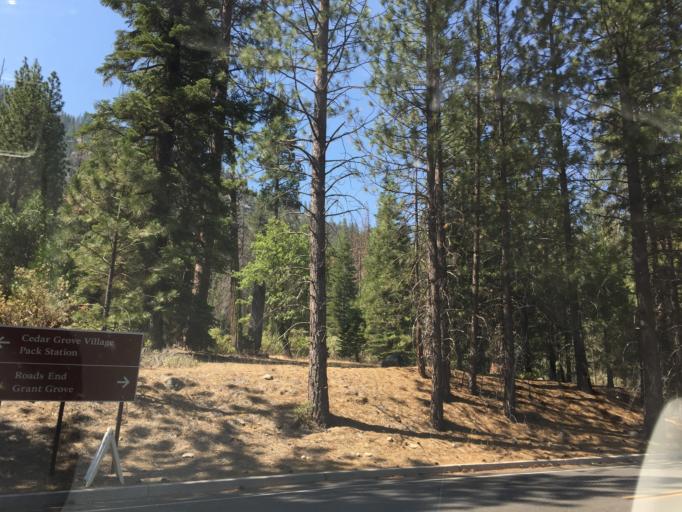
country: US
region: California
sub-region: Tulare County
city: Three Rivers
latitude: 36.7899
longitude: -118.6715
